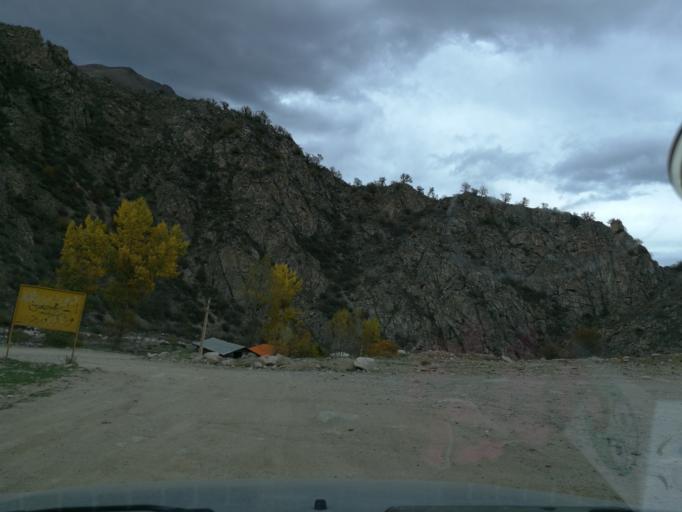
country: IR
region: Mazandaran
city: `Abbasabad
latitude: 36.4373
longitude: 51.0601
